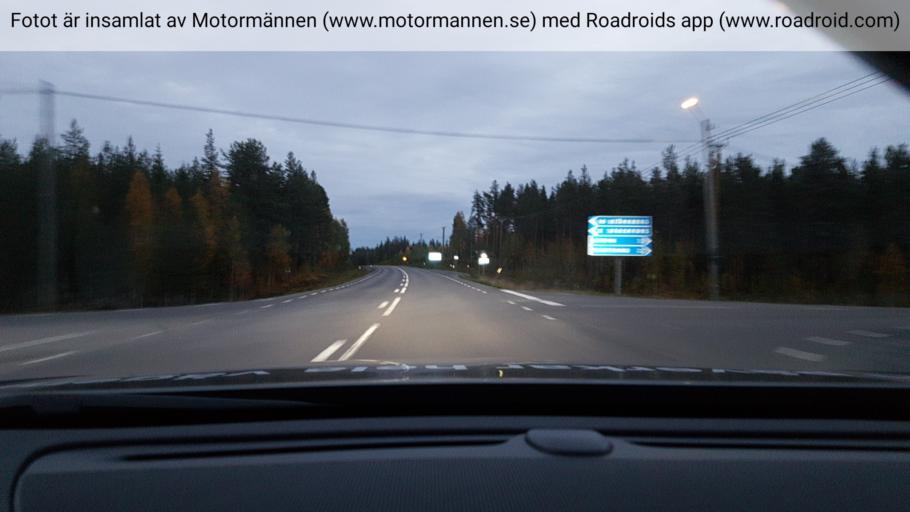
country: SE
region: Norrbotten
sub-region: Alvsbyns Kommun
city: AElvsbyn
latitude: 65.7462
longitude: 20.9283
